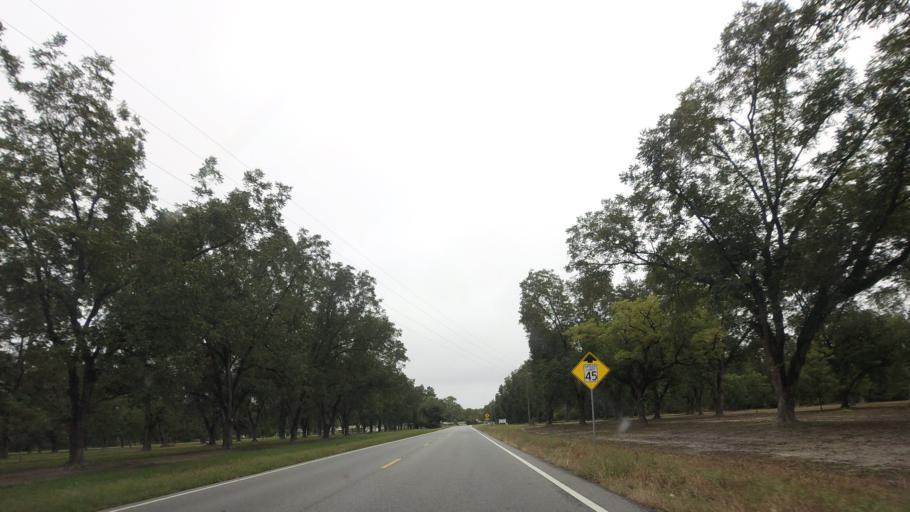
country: US
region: Georgia
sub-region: Berrien County
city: Enigma
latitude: 31.3717
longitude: -83.2263
